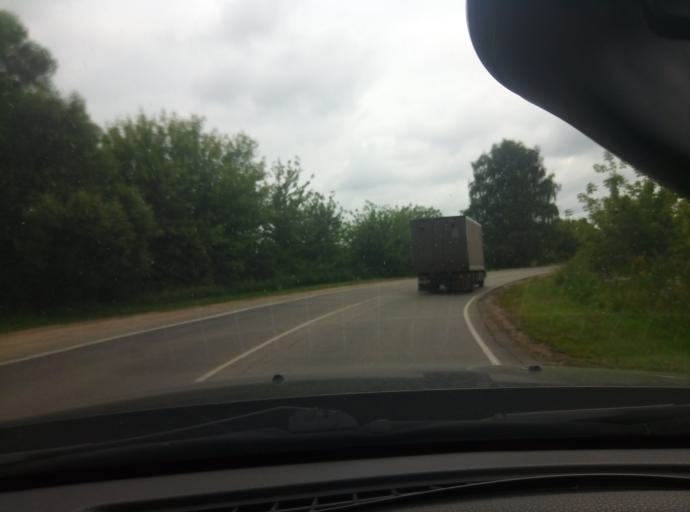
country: RU
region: Tula
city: Kimovsk
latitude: 53.9513
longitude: 38.5394
